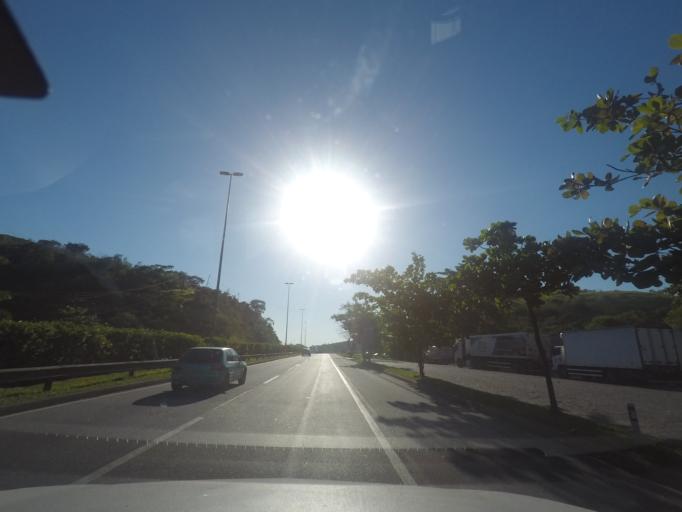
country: BR
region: Rio de Janeiro
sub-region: Petropolis
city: Petropolis
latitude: -22.6530
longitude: -43.1599
